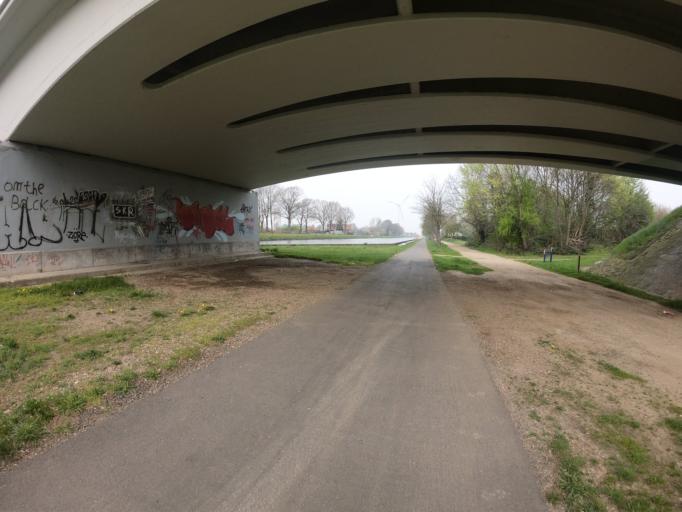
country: BE
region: Flanders
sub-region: Provincie Limburg
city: Maasmechelen
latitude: 50.9407
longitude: 5.7116
